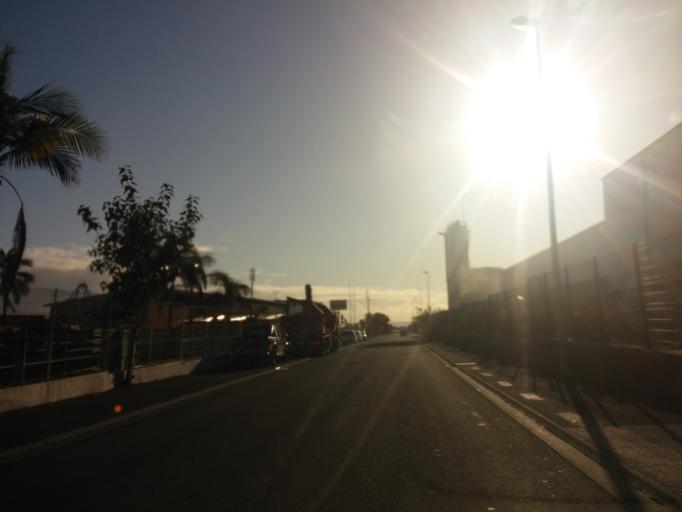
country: RE
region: Reunion
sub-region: Reunion
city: La Possession
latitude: -20.9366
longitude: 55.3170
